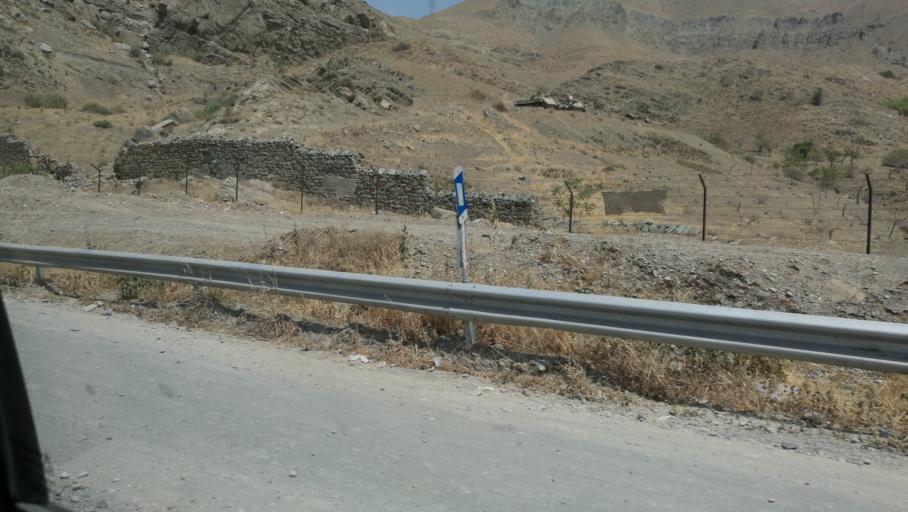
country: IR
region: Alborz
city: Karaj
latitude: 35.8272
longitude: 51.0421
